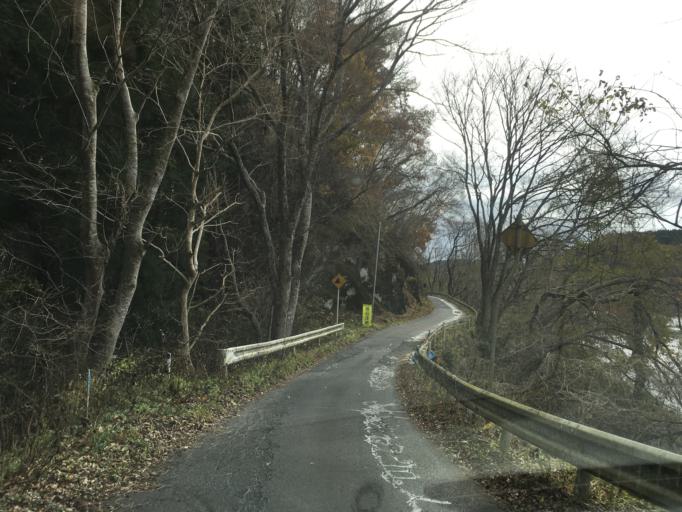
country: JP
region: Iwate
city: Ichinoseki
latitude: 38.7856
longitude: 141.2644
